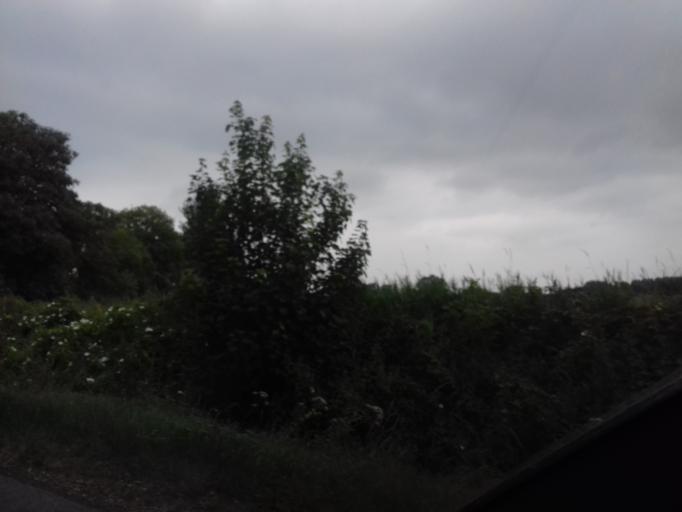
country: IE
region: Leinster
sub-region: Fingal County
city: Swords
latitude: 53.4749
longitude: -6.2301
